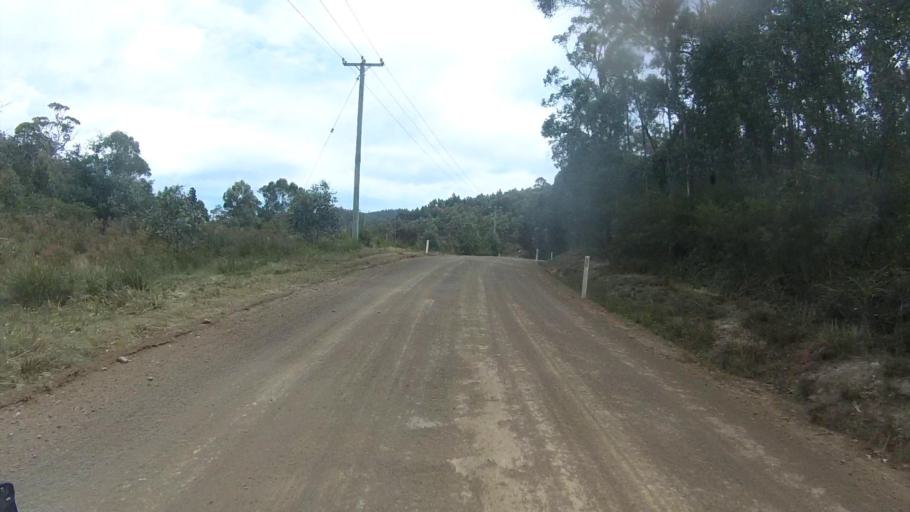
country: AU
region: Tasmania
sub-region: Sorell
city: Sorell
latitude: -42.7603
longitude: 147.8021
